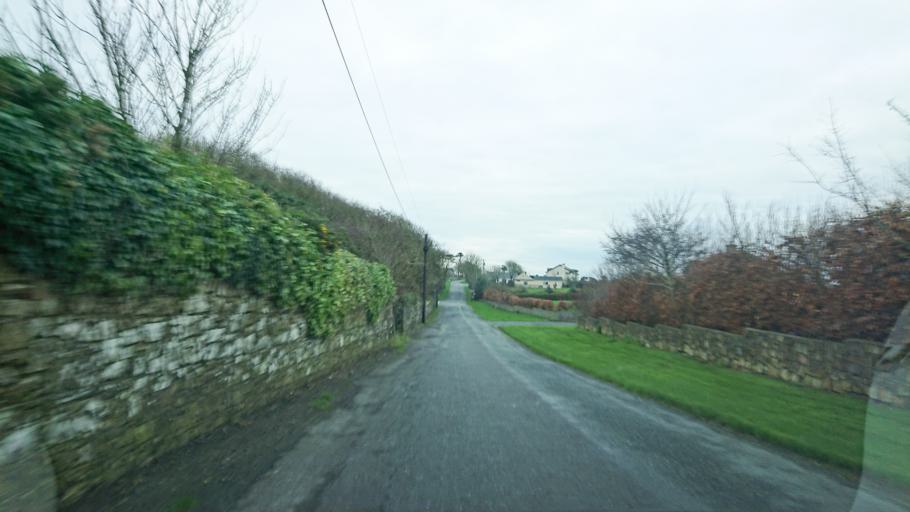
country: IE
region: Munster
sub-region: Waterford
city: Tra Mhor
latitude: 52.1458
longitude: -7.1725
